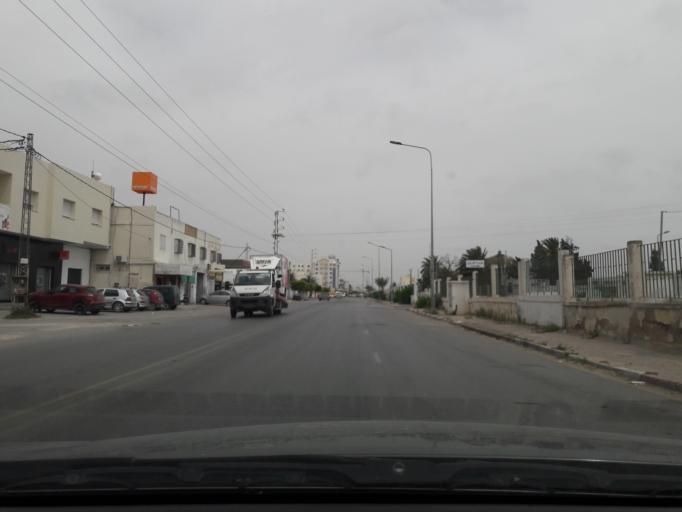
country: TN
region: Safaqis
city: Al Qarmadah
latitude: 34.7785
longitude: 10.7607
